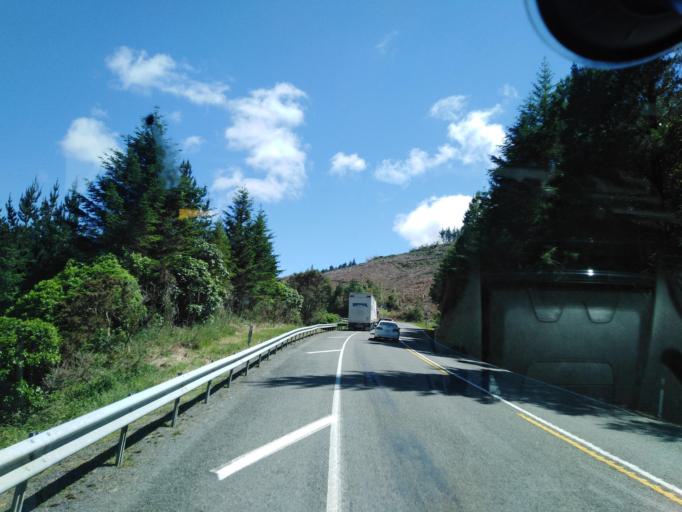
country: NZ
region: Nelson
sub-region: Nelson City
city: Nelson
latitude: -41.1953
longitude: 173.5580
